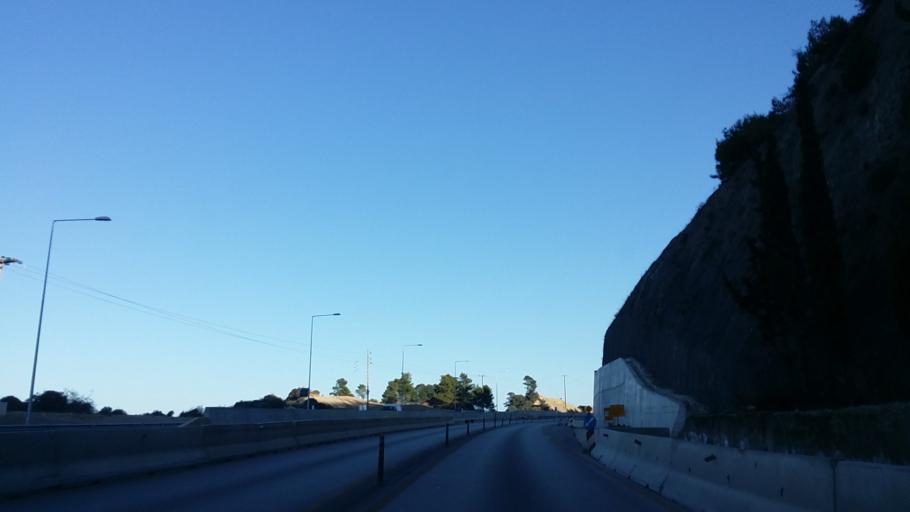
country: GR
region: West Greece
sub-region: Nomos Achaias
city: Akrata
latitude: 38.1741
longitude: 22.2486
